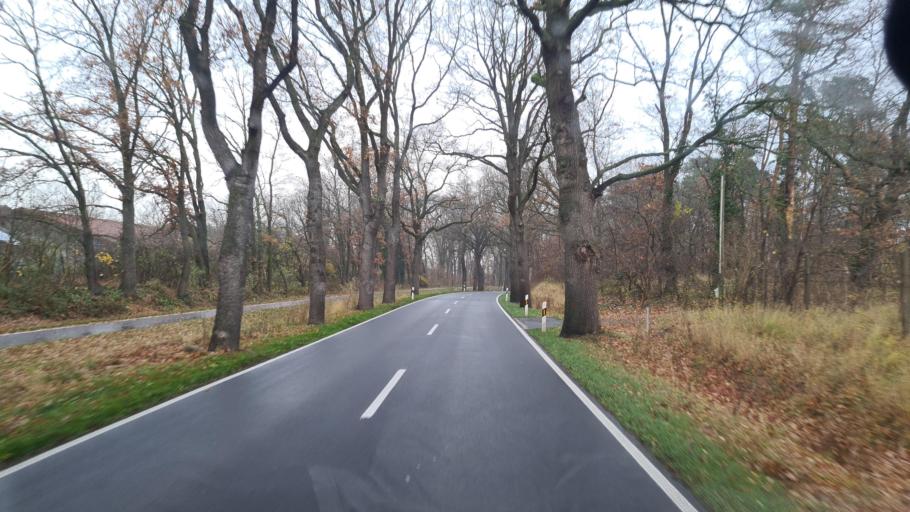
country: DE
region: Brandenburg
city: Gross Kreutz
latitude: 52.3955
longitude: 12.7677
